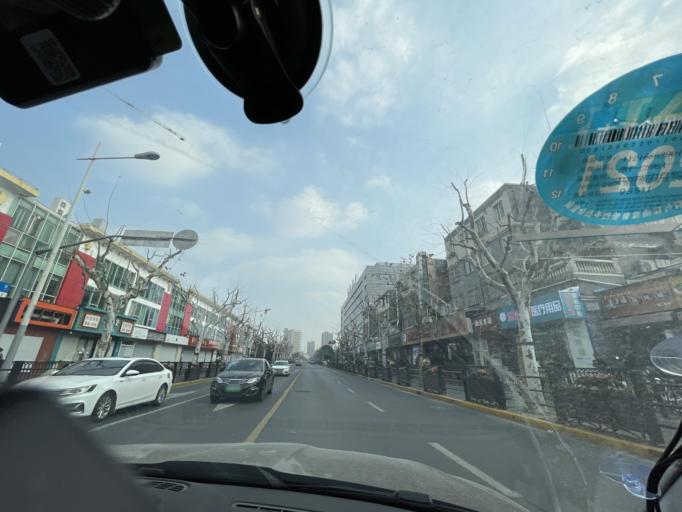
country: CN
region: Shanghai Shi
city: Yangpu
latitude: 31.3117
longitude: 121.5198
